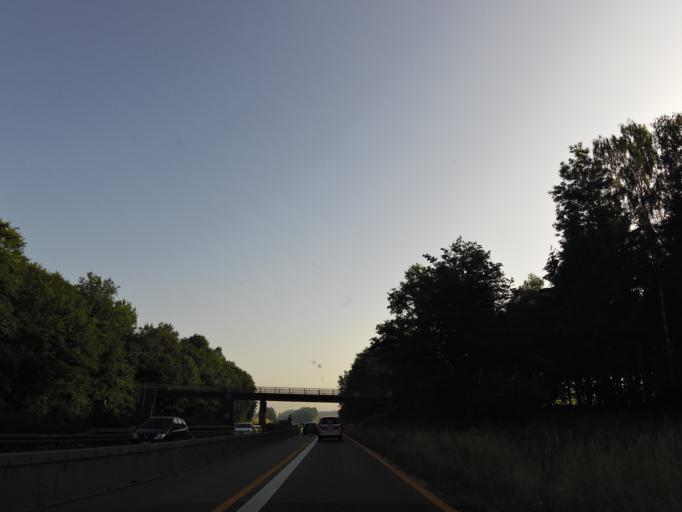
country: DE
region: Bavaria
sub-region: Swabia
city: Holzheim
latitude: 48.3731
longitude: 10.0845
